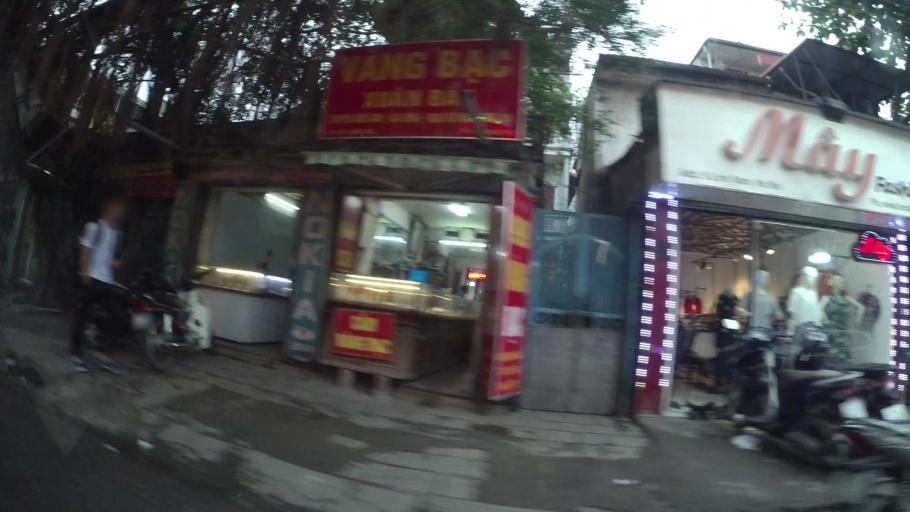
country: VN
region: Ha Noi
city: Hai BaTrung
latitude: 20.9910
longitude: 105.8641
